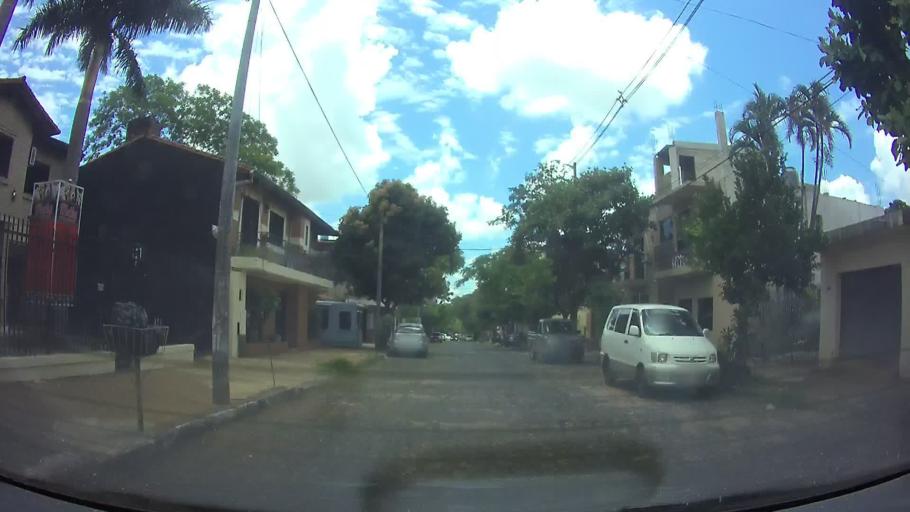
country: PY
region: Central
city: Lambare
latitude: -25.3133
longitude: -57.5946
